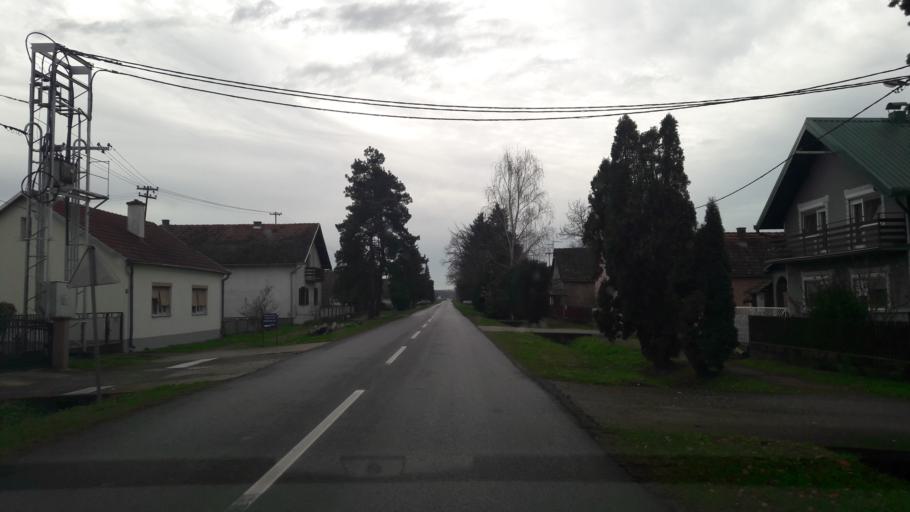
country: HR
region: Osjecko-Baranjska
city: Martin
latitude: 45.5319
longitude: 18.0599
